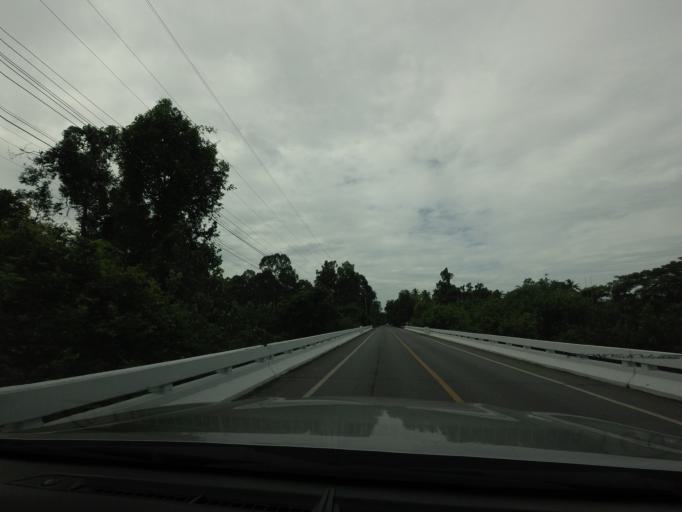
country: TH
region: Nakhon Si Thammarat
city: Phra Phrom
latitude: 8.3111
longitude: 99.9436
